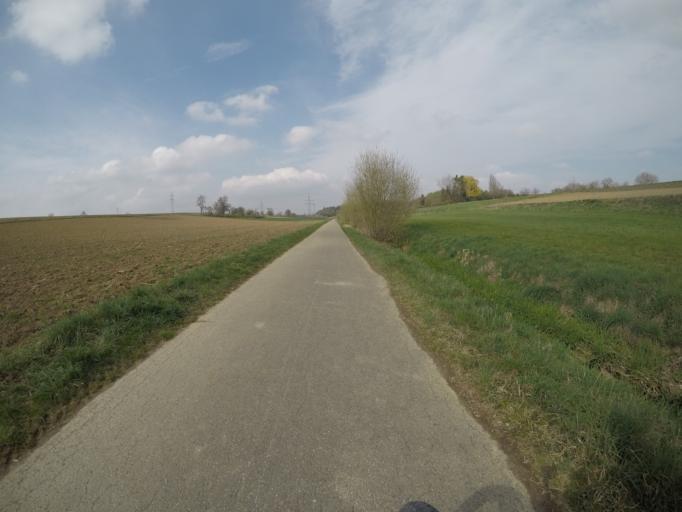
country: DE
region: Baden-Wuerttemberg
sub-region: Regierungsbezirk Stuttgart
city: Nufringen
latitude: 48.6268
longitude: 8.8788
